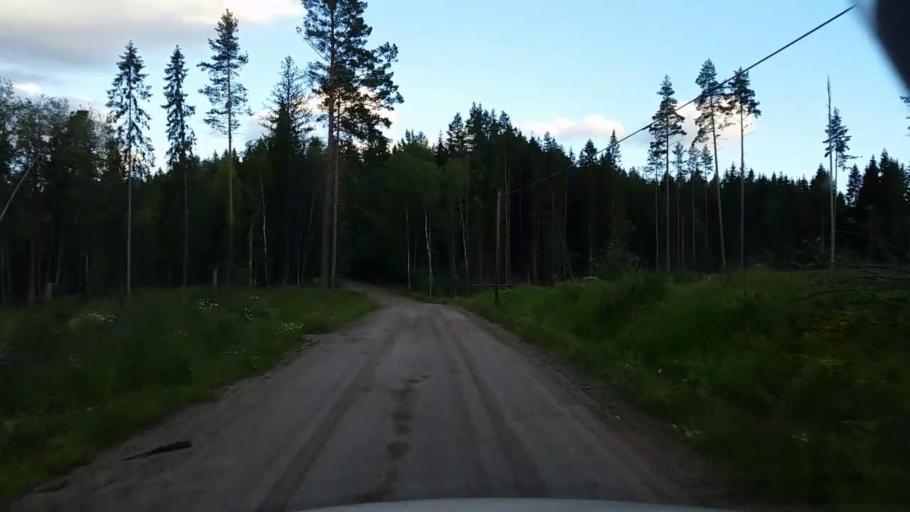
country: SE
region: Vaestmanland
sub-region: Kopings Kommun
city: Kolsva
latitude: 59.7723
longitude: 15.8826
